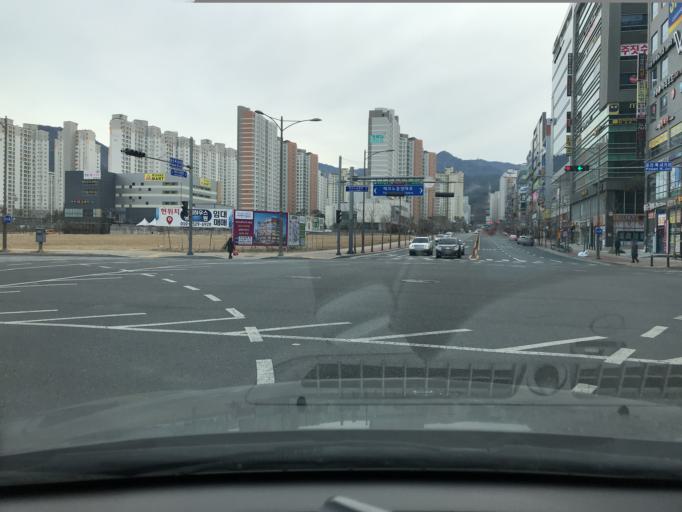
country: KR
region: Daegu
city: Hwawon
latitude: 35.6936
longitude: 128.4576
